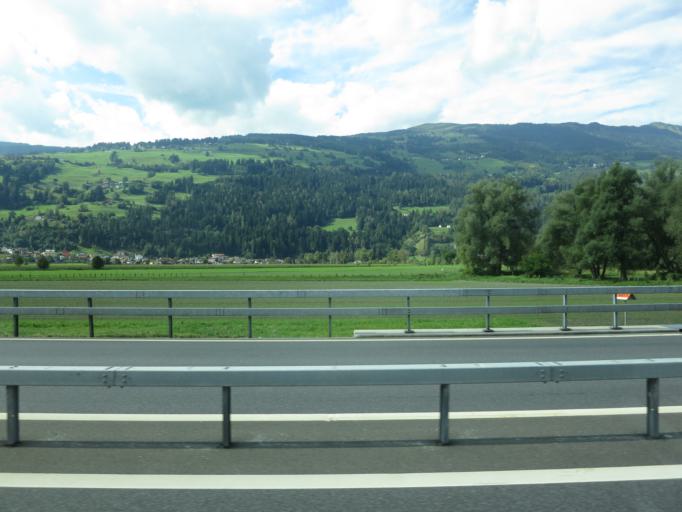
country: CH
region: Grisons
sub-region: Hinterrhein District
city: Cazis
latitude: 46.7257
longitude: 9.4401
